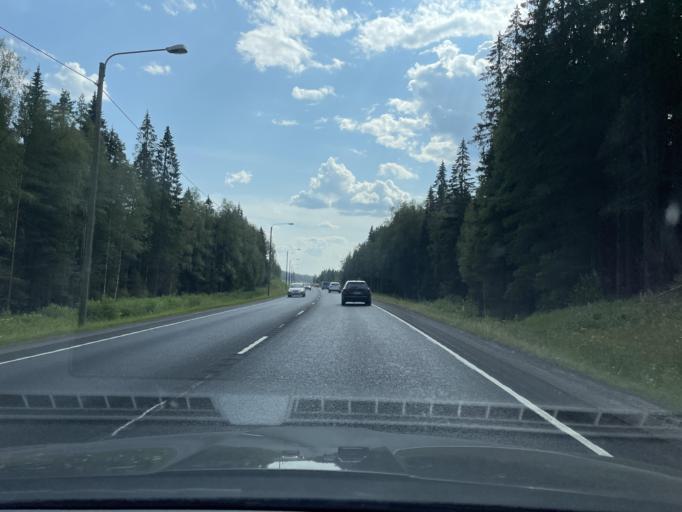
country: FI
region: Central Finland
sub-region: Jyvaeskylae
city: Muurame
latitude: 62.1558
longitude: 25.6758
